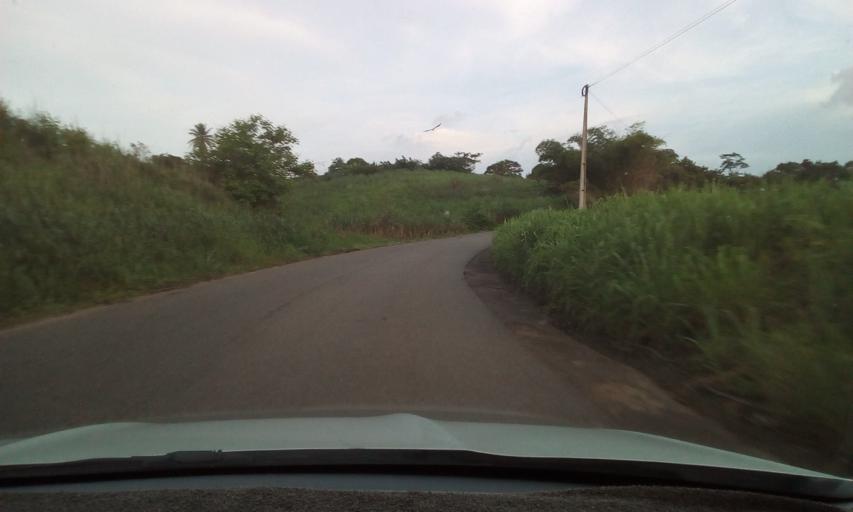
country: BR
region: Pernambuco
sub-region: Condado
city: Condado
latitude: -7.5993
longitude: -35.2138
